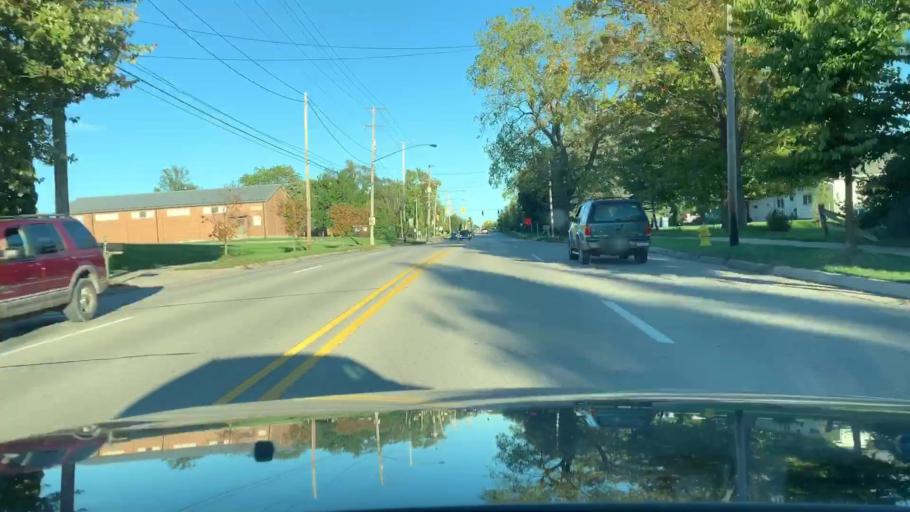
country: US
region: Michigan
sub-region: Kent County
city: East Grand Rapids
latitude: 42.9844
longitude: -85.6123
